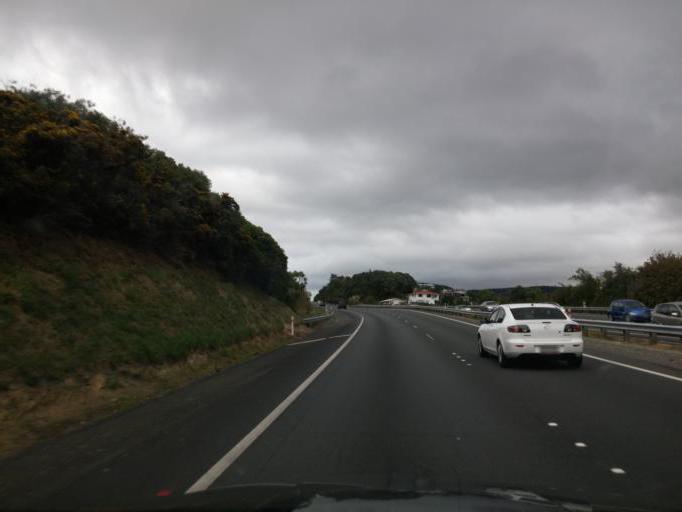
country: NZ
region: Wellington
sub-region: Porirua City
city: Porirua
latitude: -41.1679
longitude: 174.8325
